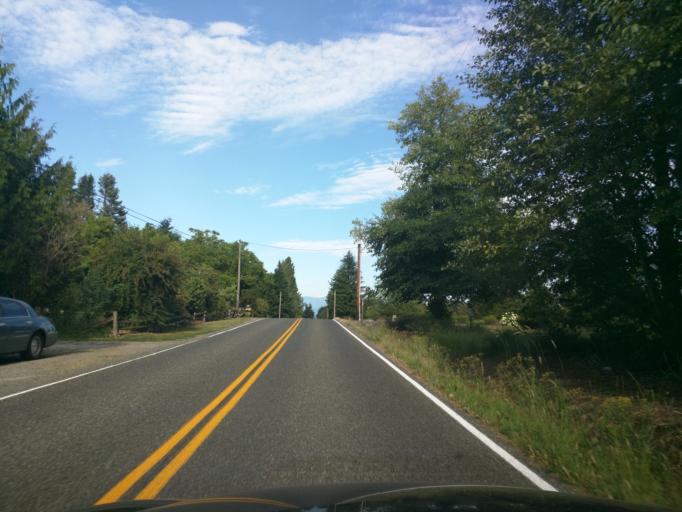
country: CA
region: British Columbia
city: Aldergrove
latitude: 48.9933
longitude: -122.5270
